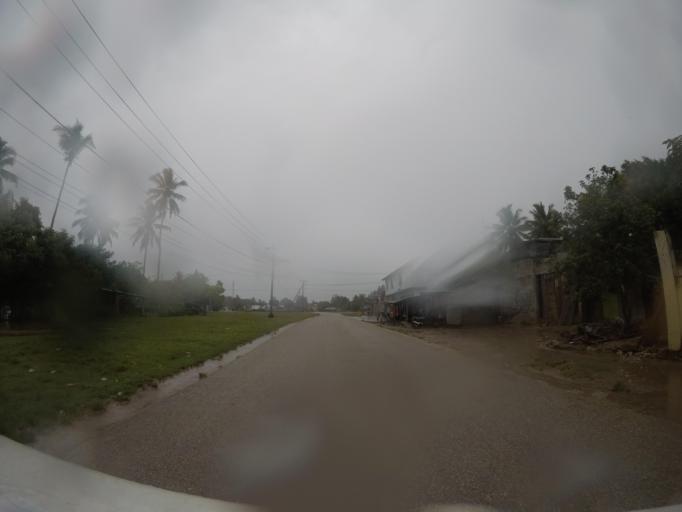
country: TL
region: Lautem
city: Lospalos
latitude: -8.5213
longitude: 127.0000
